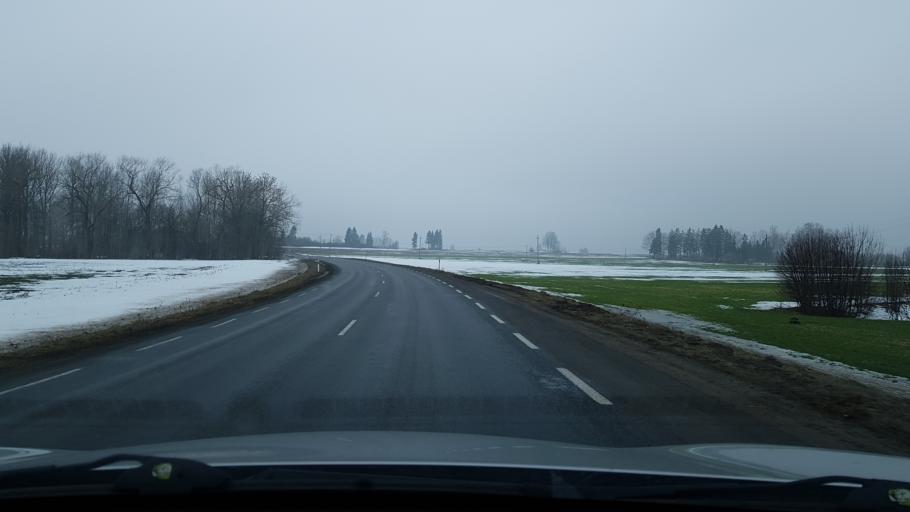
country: EE
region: Viljandimaa
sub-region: Viiratsi vald
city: Viiratsi
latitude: 58.2499
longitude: 25.8420
